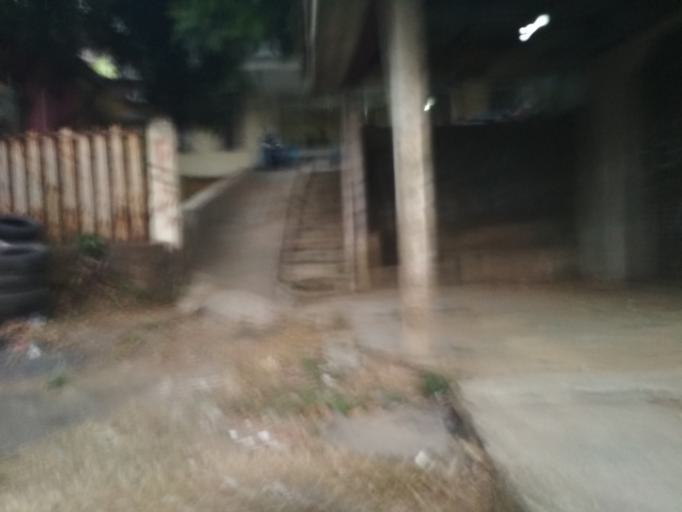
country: ID
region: West Java
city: Caringin
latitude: -6.7175
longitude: 106.8201
